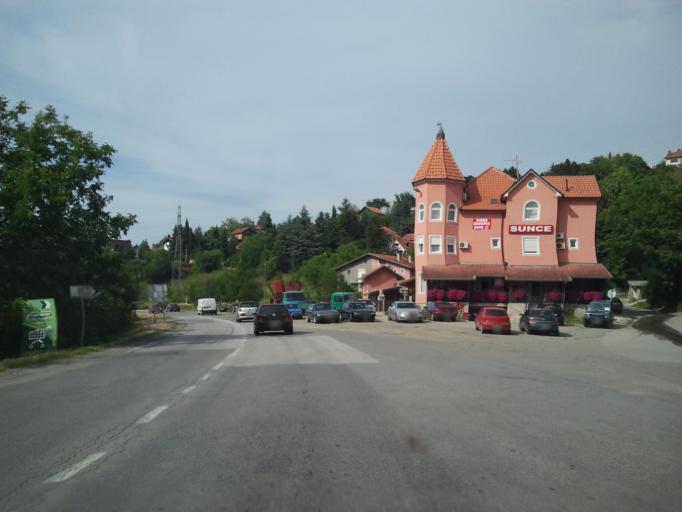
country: RS
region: Autonomna Pokrajina Vojvodina
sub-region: Juznobacki Okrug
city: Novi Sad
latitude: 45.2063
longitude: 19.8441
